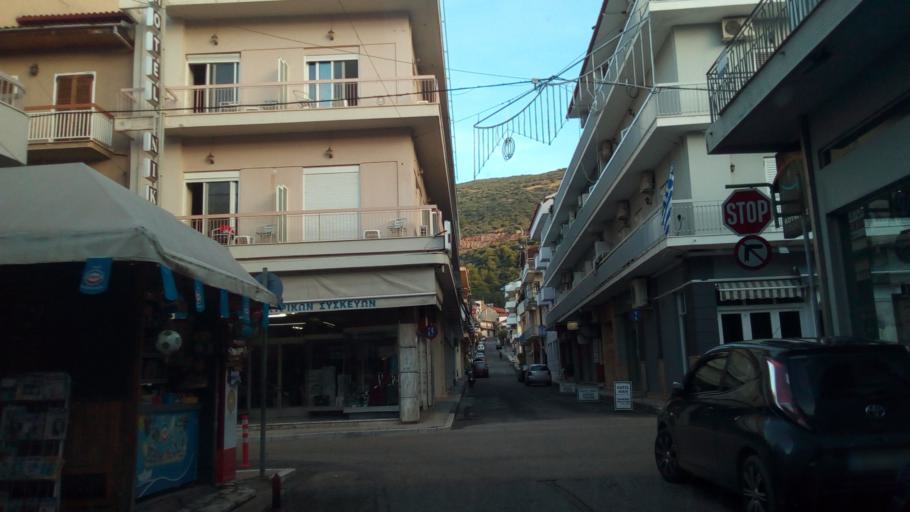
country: GR
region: West Greece
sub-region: Nomos Aitolias kai Akarnanias
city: Nafpaktos
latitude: 38.3942
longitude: 21.8328
